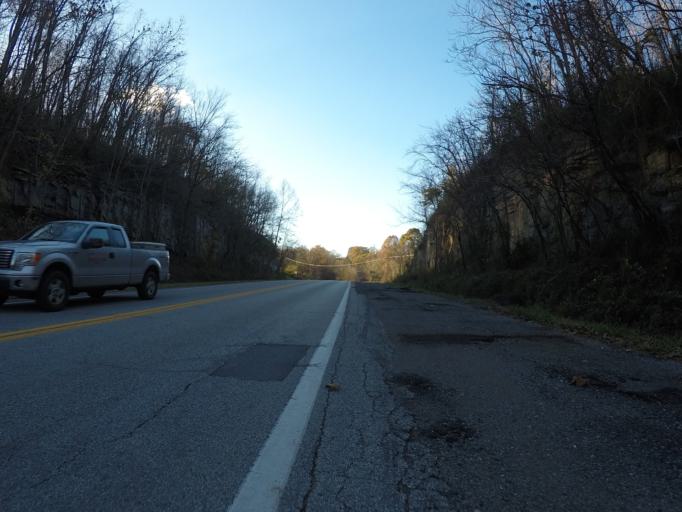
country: US
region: West Virginia
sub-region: Wayne County
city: Ceredo
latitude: 38.3826
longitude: -82.5658
